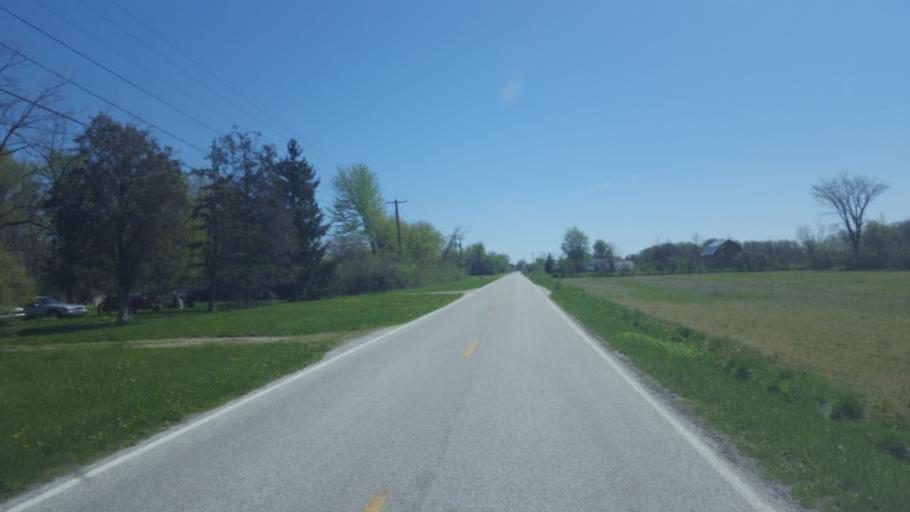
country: US
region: Ohio
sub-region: Ottawa County
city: Oak Harbor
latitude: 41.4936
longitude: -83.0987
